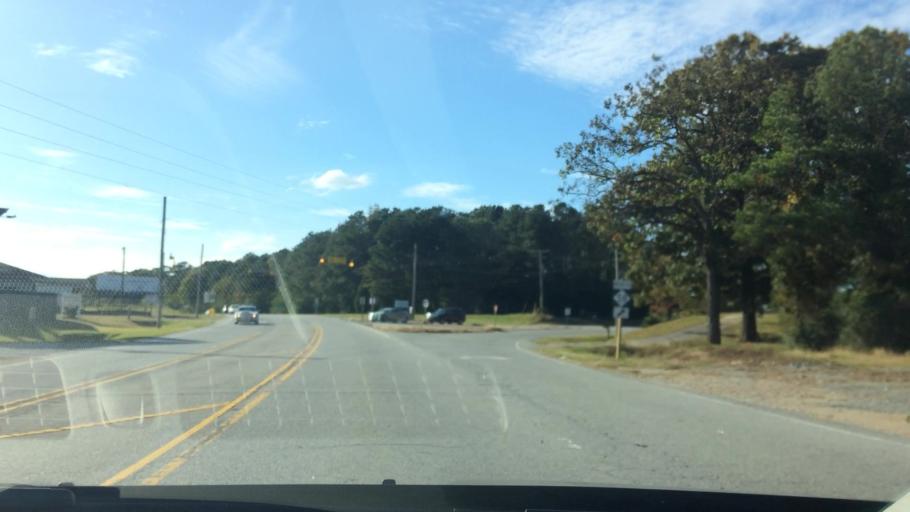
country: US
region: North Carolina
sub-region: Greene County
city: Snow Hill
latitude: 35.4594
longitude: -77.7031
